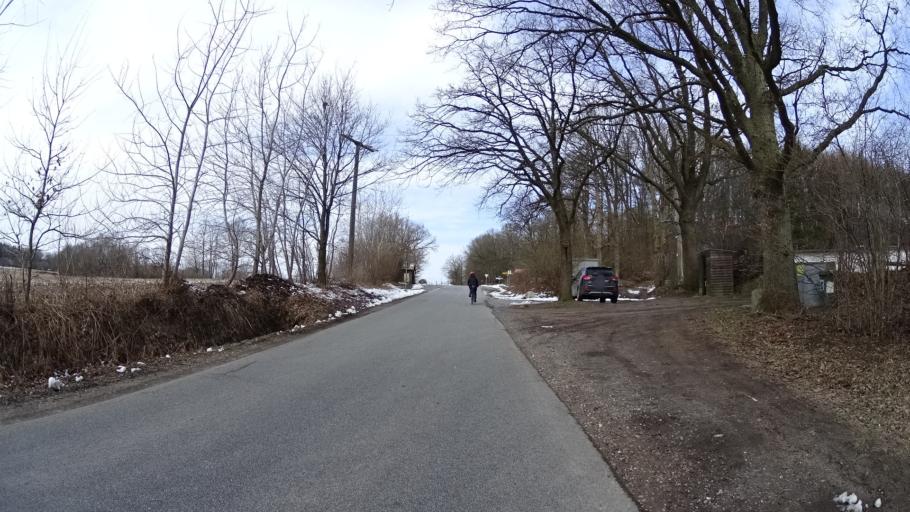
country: DE
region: Schleswig-Holstein
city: Loptin
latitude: 54.1937
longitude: 10.2308
